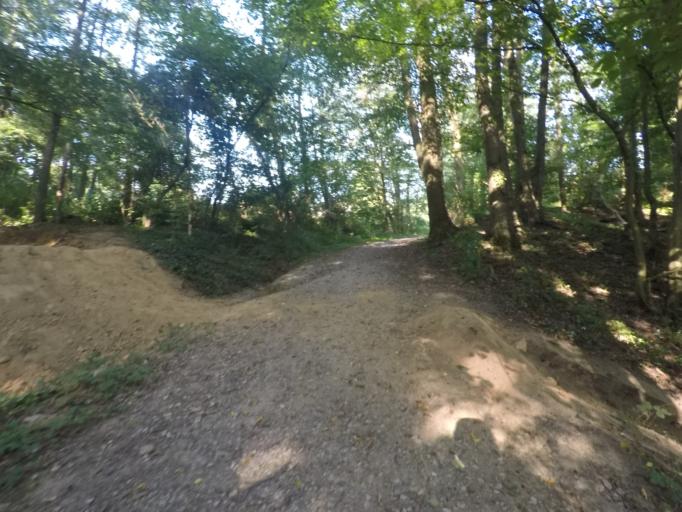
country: DE
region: North Rhine-Westphalia
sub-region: Regierungsbezirk Detmold
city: Hiddenhausen
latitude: 52.1222
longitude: 8.6265
